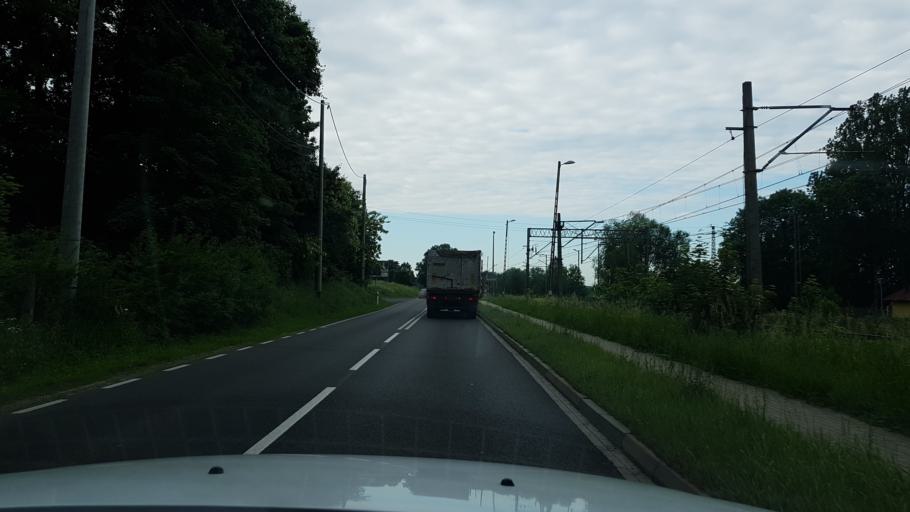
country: PL
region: West Pomeranian Voivodeship
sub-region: Powiat gryfinski
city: Gryfino
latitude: 53.3025
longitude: 14.5270
